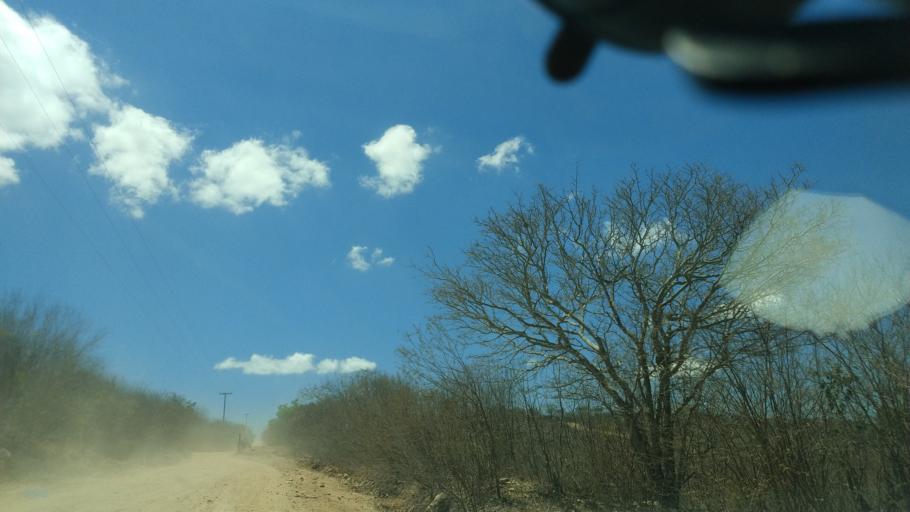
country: BR
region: Rio Grande do Norte
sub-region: Cerro Cora
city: Cerro Cora
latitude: -6.0145
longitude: -36.3274
